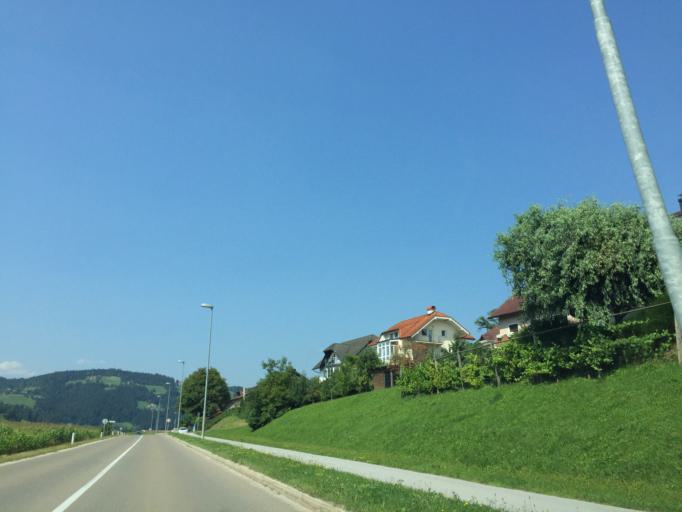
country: SI
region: Slovenj Gradec
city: Slovenj Gradec
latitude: 46.4955
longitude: 15.0718
